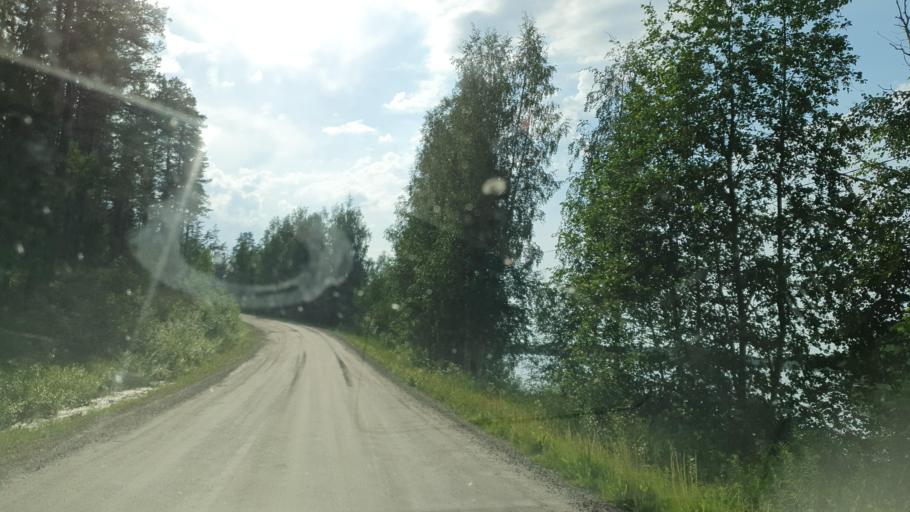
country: FI
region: Kainuu
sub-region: Kehys-Kainuu
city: Kuhmo
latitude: 64.0967
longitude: 29.6127
